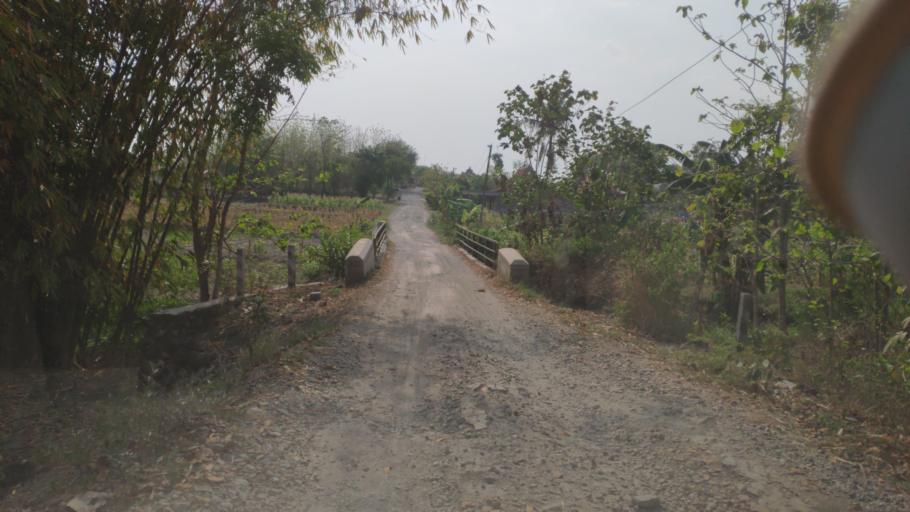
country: ID
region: Central Java
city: Randublatung
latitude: -7.2859
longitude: 111.2593
